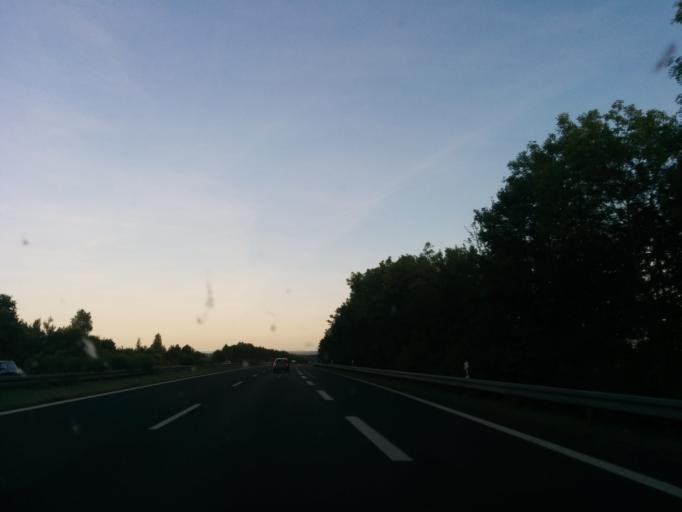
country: DE
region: Bavaria
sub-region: Regierungsbezirk Unterfranken
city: Biebelried
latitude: 49.7622
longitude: 10.1043
